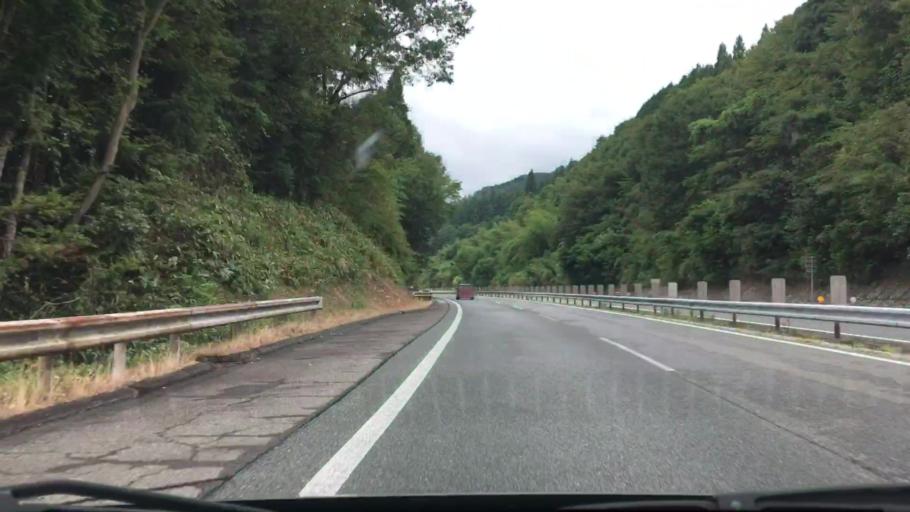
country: JP
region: Okayama
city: Niimi
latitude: 34.9572
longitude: 133.3295
